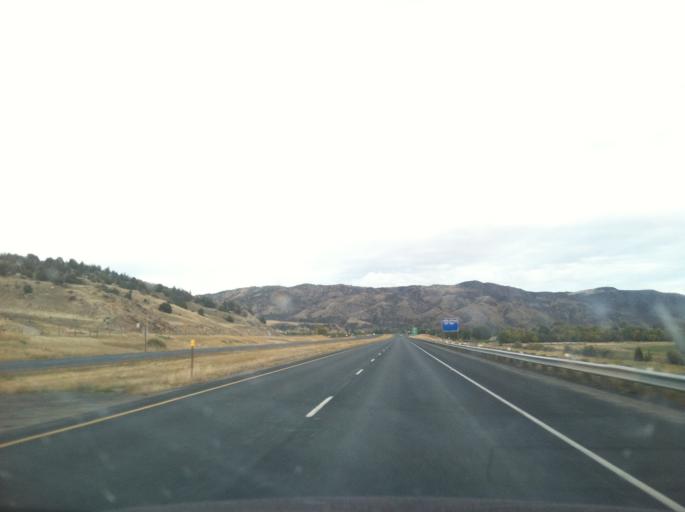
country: US
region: Montana
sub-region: Jefferson County
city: Whitehall
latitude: 45.8714
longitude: -111.9663
